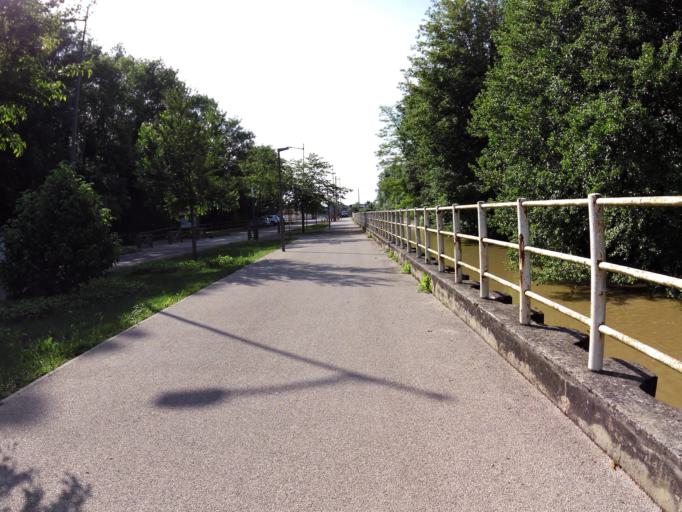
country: FR
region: Champagne-Ardenne
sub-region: Departement de l'Aube
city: Troyes
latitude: 48.2870
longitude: 4.0863
